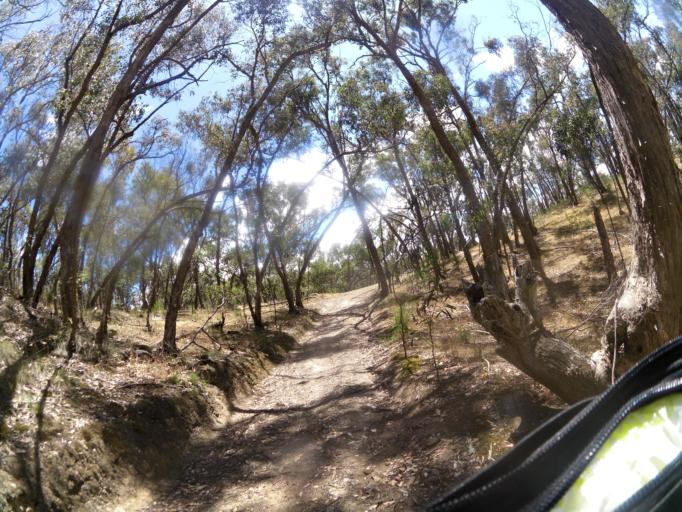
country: AU
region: Victoria
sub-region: Mount Alexander
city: Castlemaine
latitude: -37.0630
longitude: 144.2664
